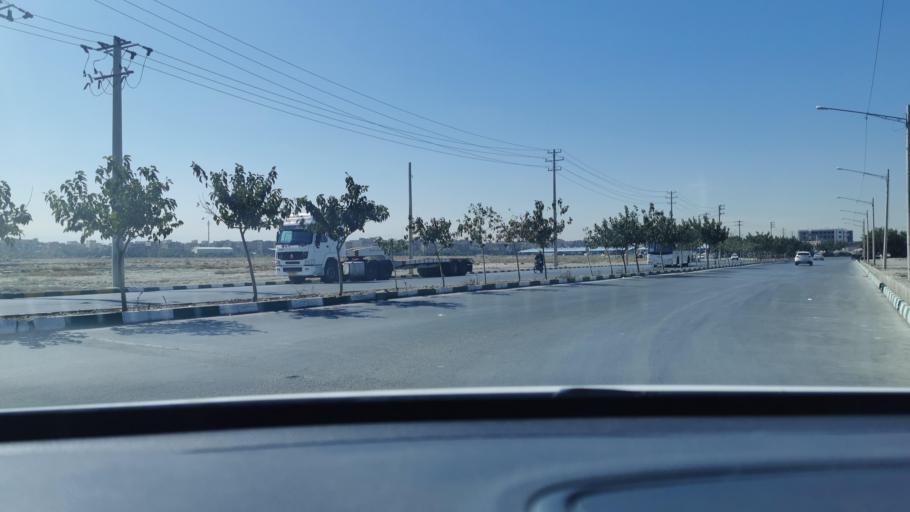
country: IR
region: Razavi Khorasan
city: Mashhad
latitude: 36.3357
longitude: 59.6254
